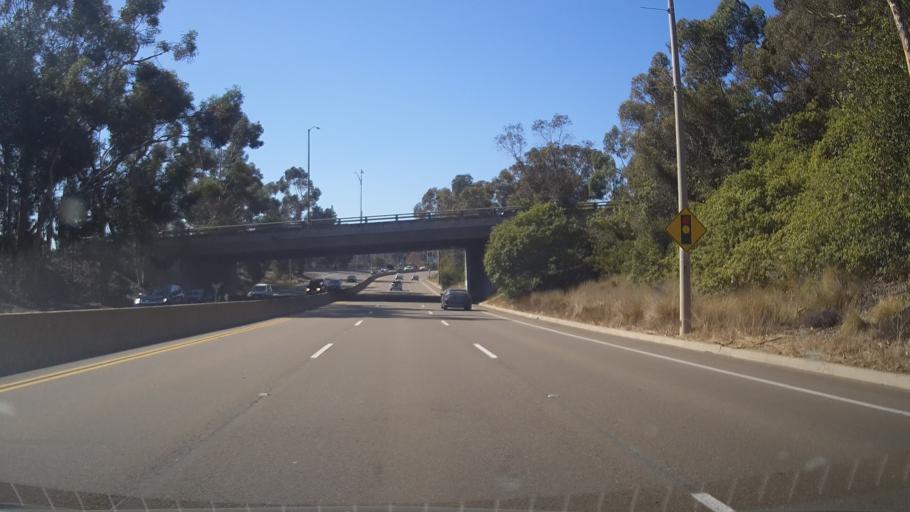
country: US
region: California
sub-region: San Diego County
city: San Diego
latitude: 32.7871
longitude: -117.1193
